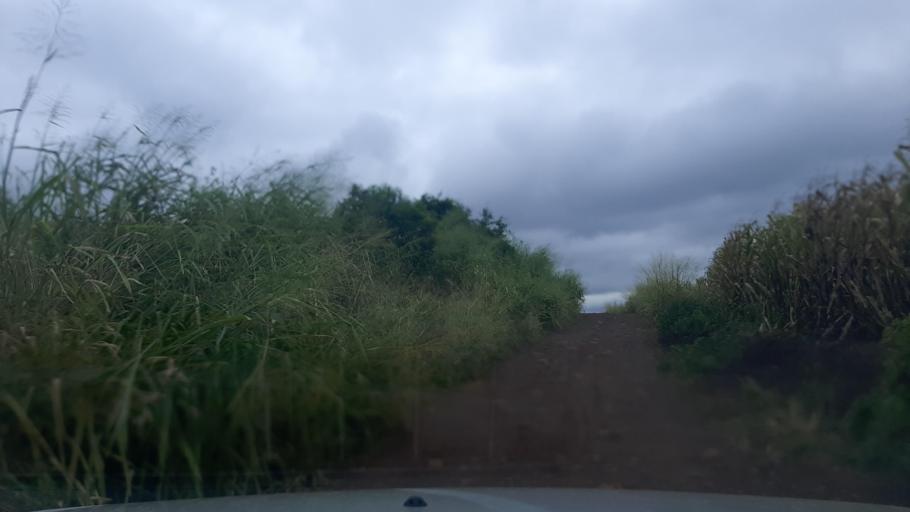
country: BR
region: Parana
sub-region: Ampere
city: Ampere
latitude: -26.0500
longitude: -53.5338
